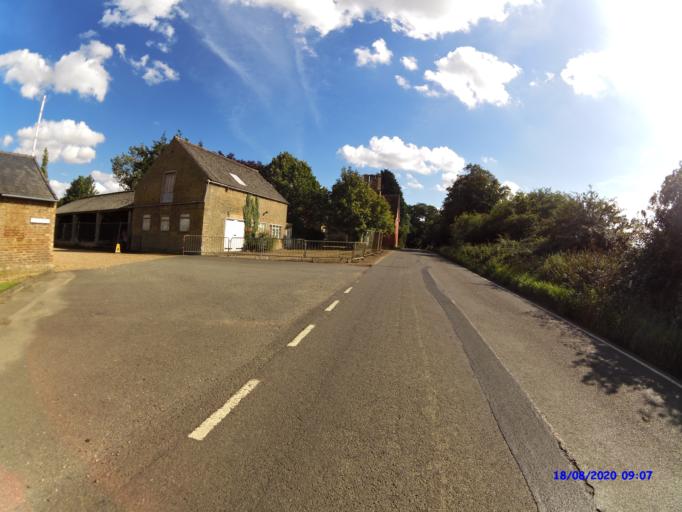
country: GB
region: England
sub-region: Cambridgeshire
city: Ramsey
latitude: 52.4691
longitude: -0.0948
